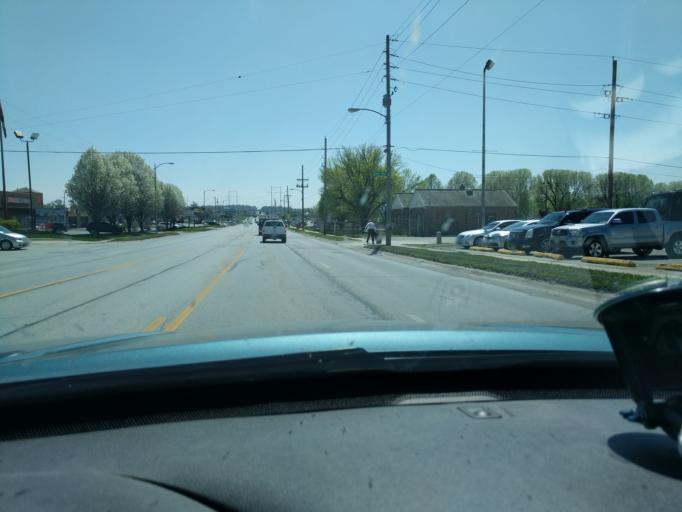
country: US
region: Nebraska
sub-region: Douglas County
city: Ralston
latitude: 41.2328
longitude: -96.0431
